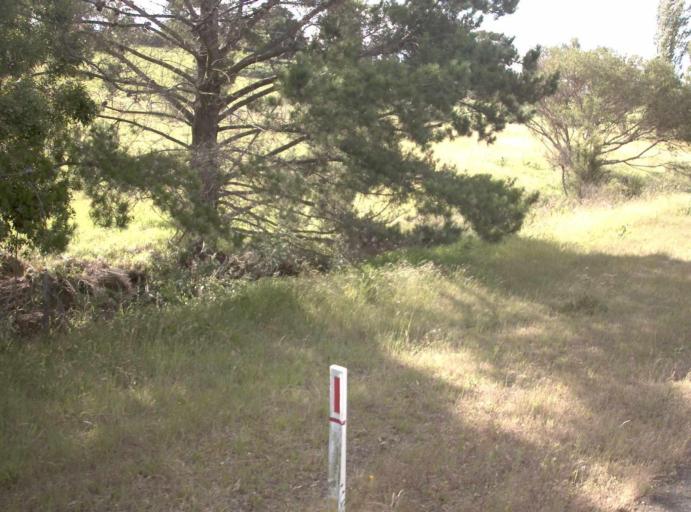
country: AU
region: Victoria
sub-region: Latrobe
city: Moe
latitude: -38.2003
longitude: 146.3280
